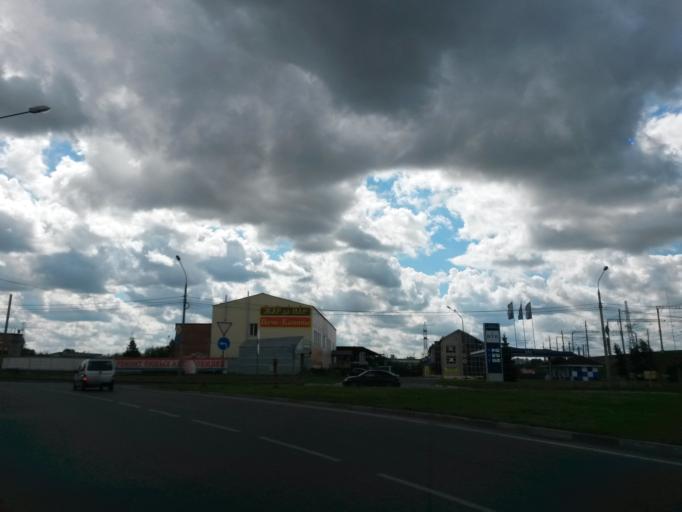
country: RU
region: Jaroslavl
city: Yaroslavl
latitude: 57.6187
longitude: 39.8486
